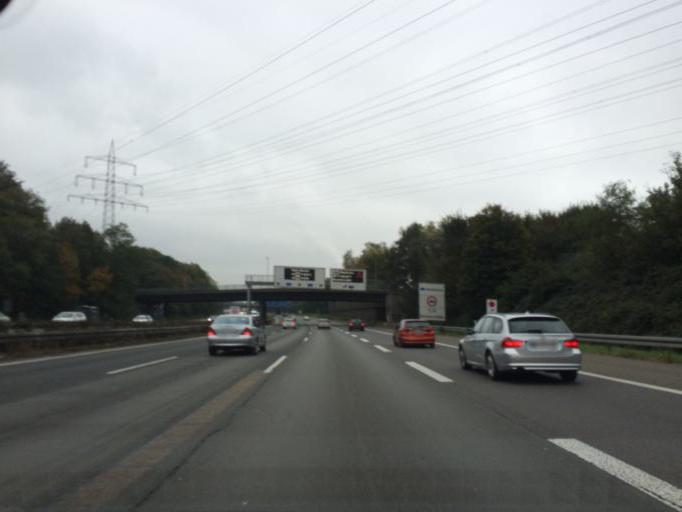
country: DE
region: North Rhine-Westphalia
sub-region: Regierungsbezirk Koln
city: Leverkusen
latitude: 51.0543
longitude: 6.9930
